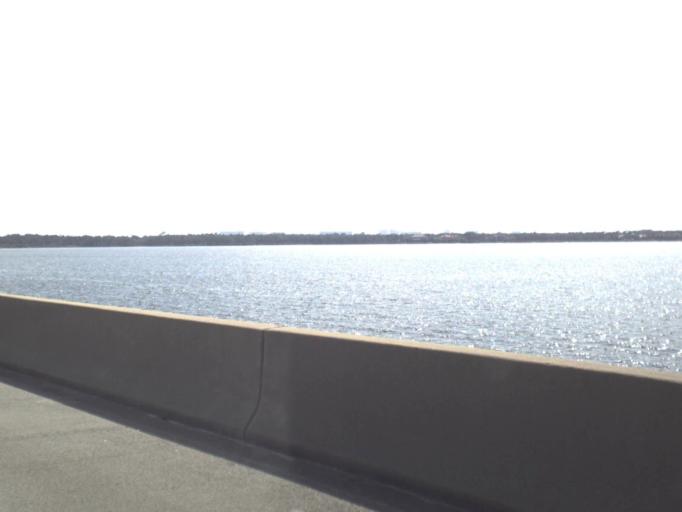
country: US
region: Florida
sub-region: Walton County
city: Miramar Beach
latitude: 30.4147
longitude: -86.4223
